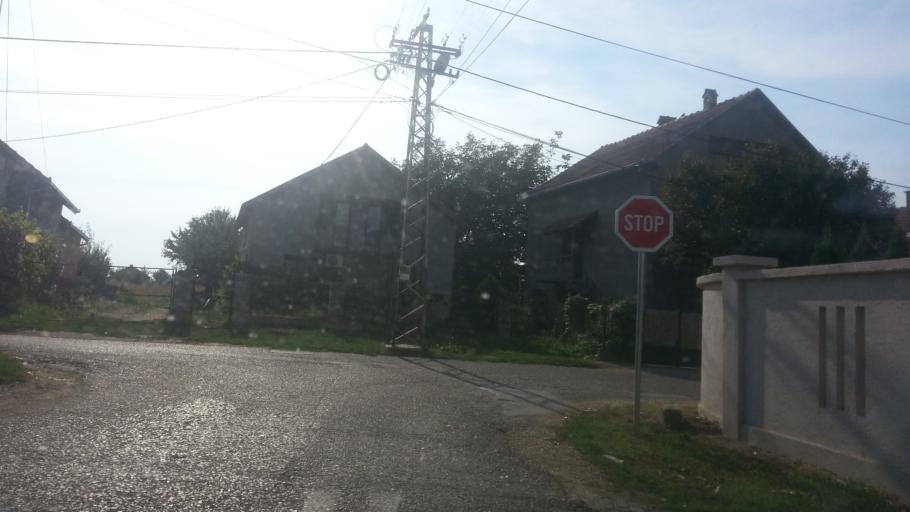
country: RS
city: Novi Banovci
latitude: 44.9501
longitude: 20.2811
